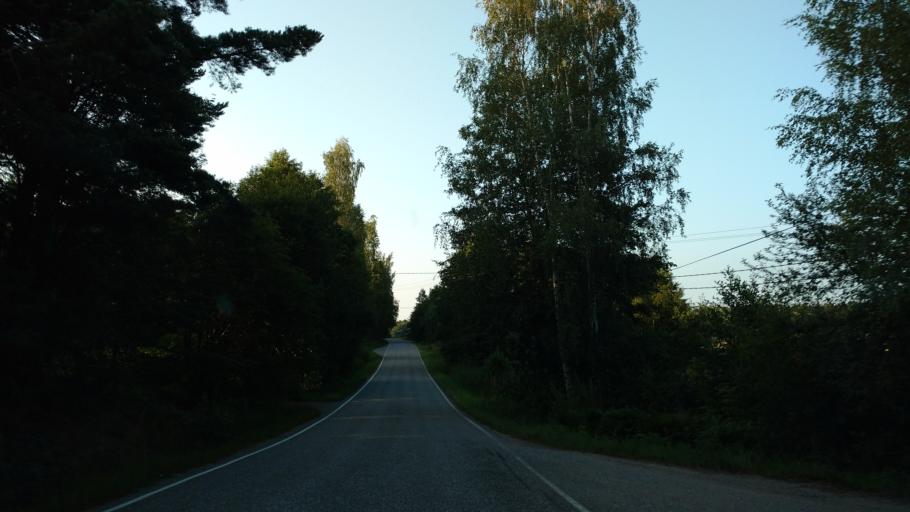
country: FI
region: Varsinais-Suomi
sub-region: Aboland-Turunmaa
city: Dragsfjaerd
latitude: 60.0158
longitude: 22.4586
